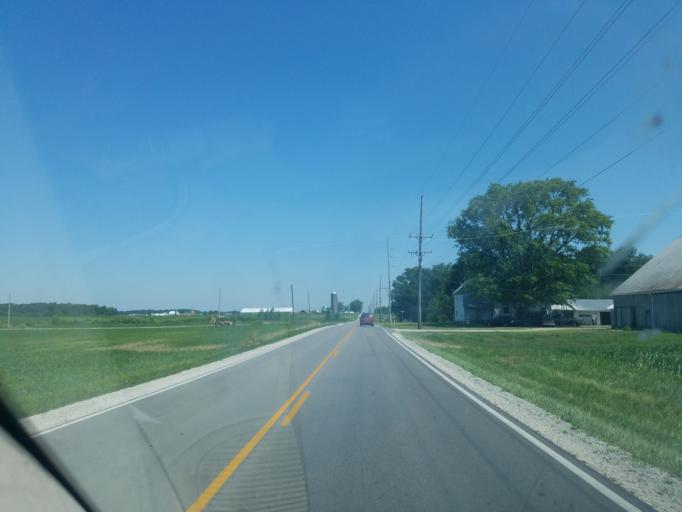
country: US
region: Ohio
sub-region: Mercer County
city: Saint Henry
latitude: 40.4347
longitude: -84.6482
